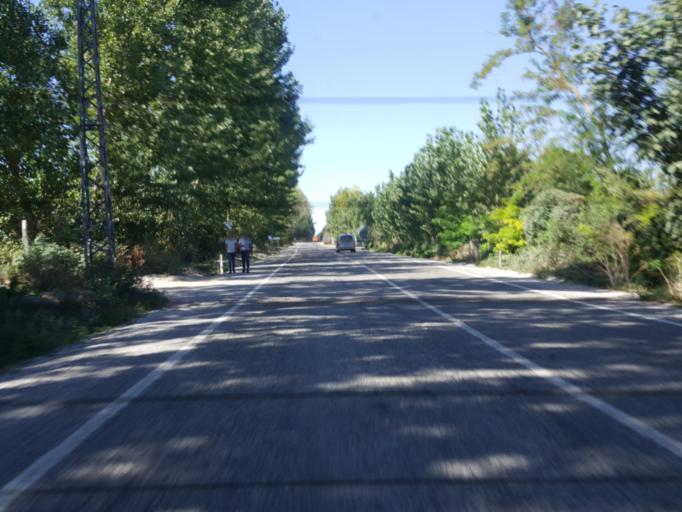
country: TR
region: Tokat
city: Pazar
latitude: 40.2702
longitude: 36.2439
